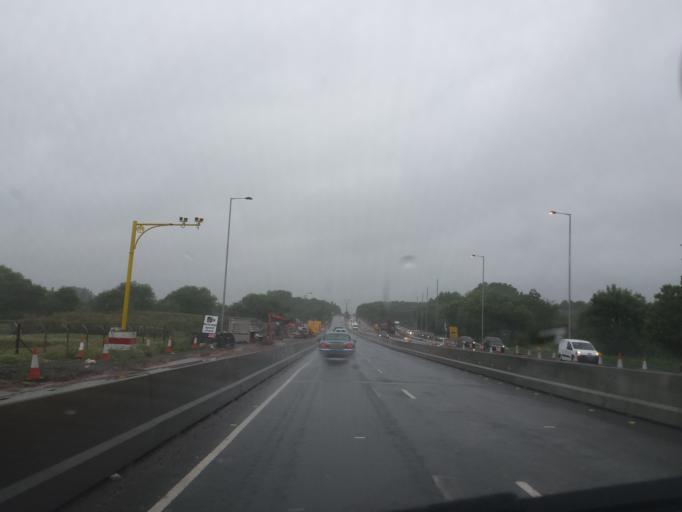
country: GB
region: England
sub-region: Coventry
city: Coventry
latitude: 52.3773
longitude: -1.4918
